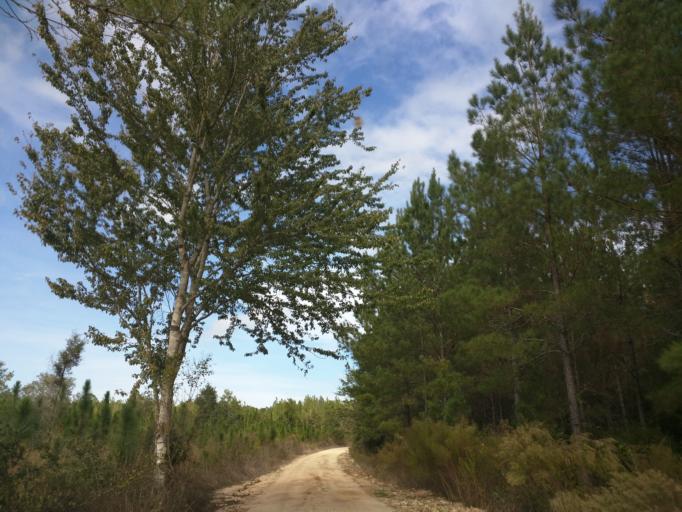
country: US
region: Florida
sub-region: Escambia County
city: Cantonment
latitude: 30.5367
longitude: -87.4367
